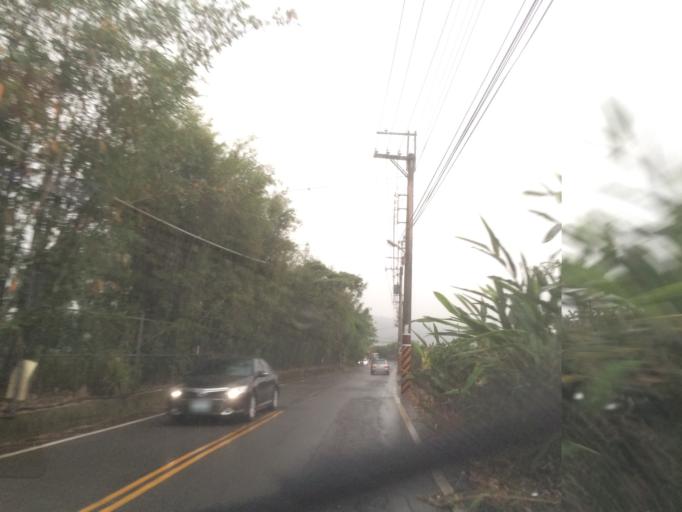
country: TW
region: Taiwan
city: Fengyuan
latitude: 24.1994
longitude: 120.8002
